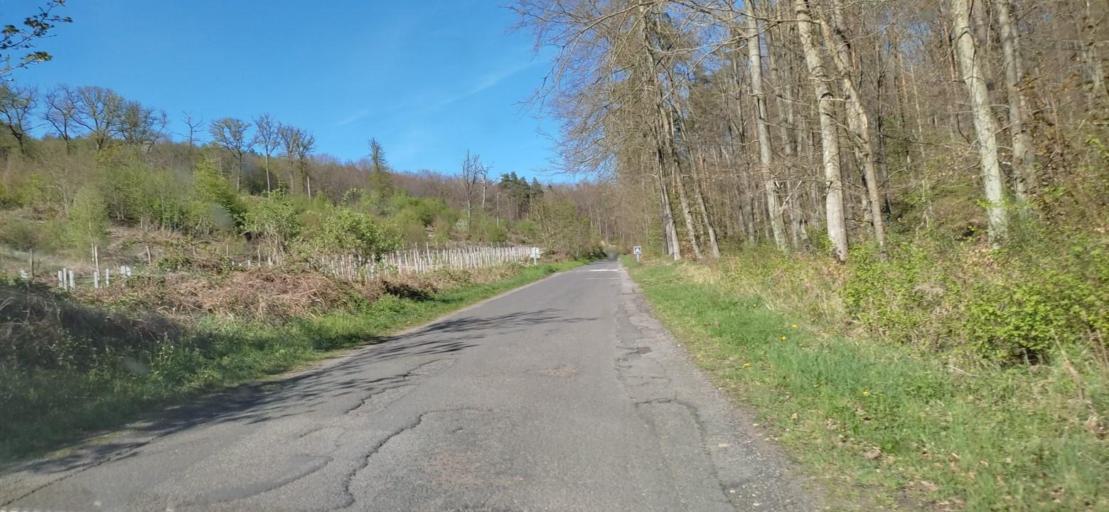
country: FR
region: Picardie
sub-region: Departement de l'Oise
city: Le Plessis-Brion
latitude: 49.4373
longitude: 2.9124
